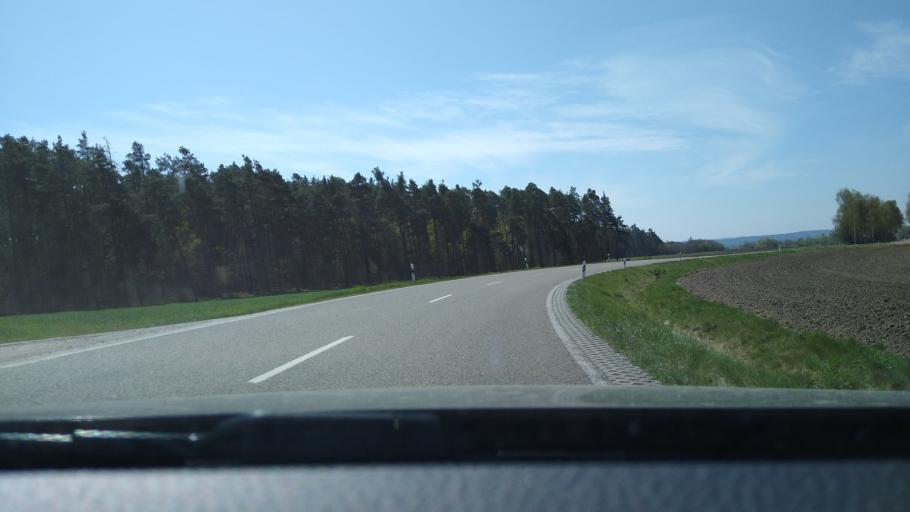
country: DE
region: Bavaria
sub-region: Regierungsbezirk Mittelfranken
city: Merkendorf
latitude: 49.1876
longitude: 10.7228
